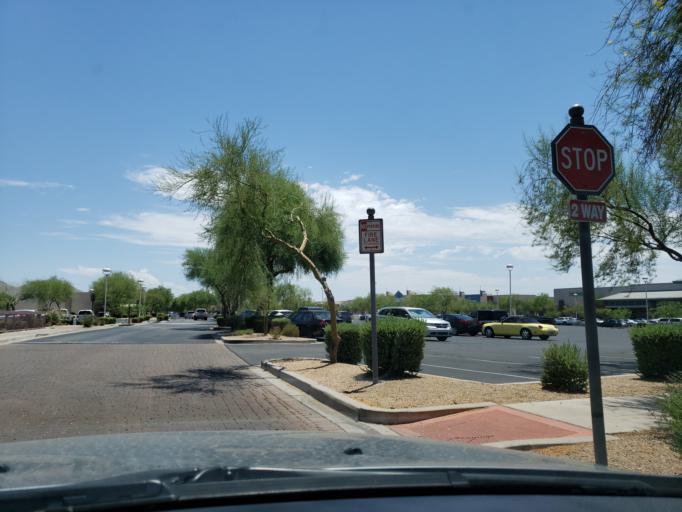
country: US
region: Arizona
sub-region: Maricopa County
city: Paradise Valley
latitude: 33.6363
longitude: -111.9202
